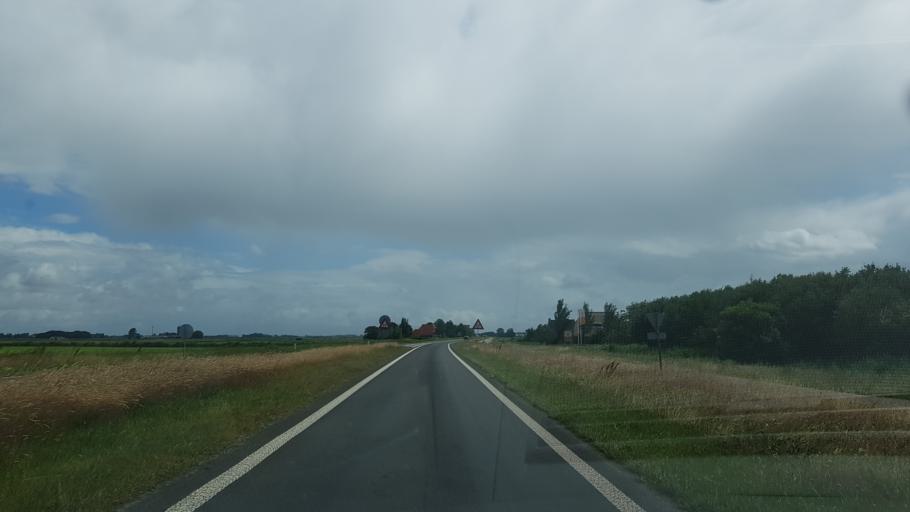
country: NL
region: Friesland
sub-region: Gemeente Ferwerderadiel
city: Burdaard
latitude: 53.2827
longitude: 5.9078
